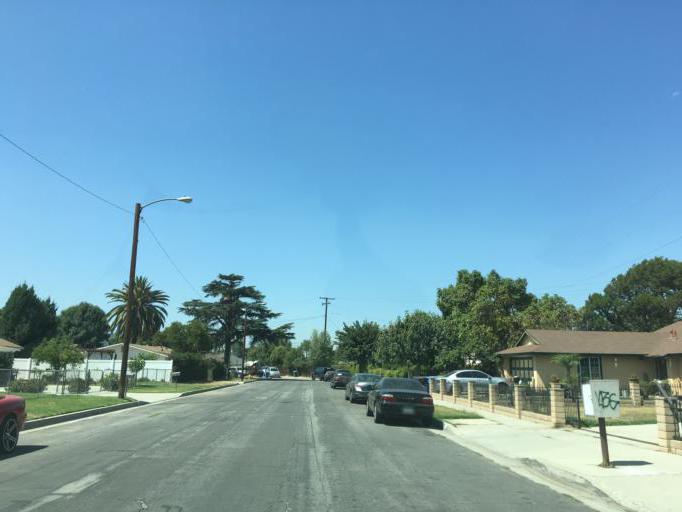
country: US
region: California
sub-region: Los Angeles County
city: Avocado Heights
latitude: 34.0476
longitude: -118.0053
